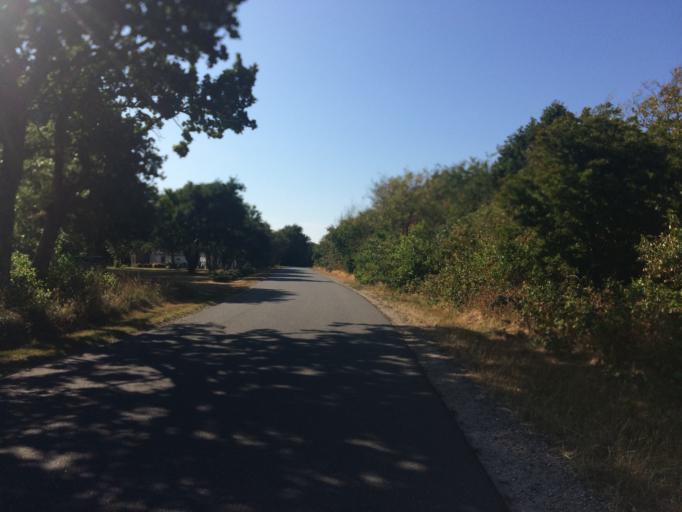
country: DK
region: Central Jutland
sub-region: Holstebro Kommune
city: Vinderup
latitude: 56.5419
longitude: 8.7765
